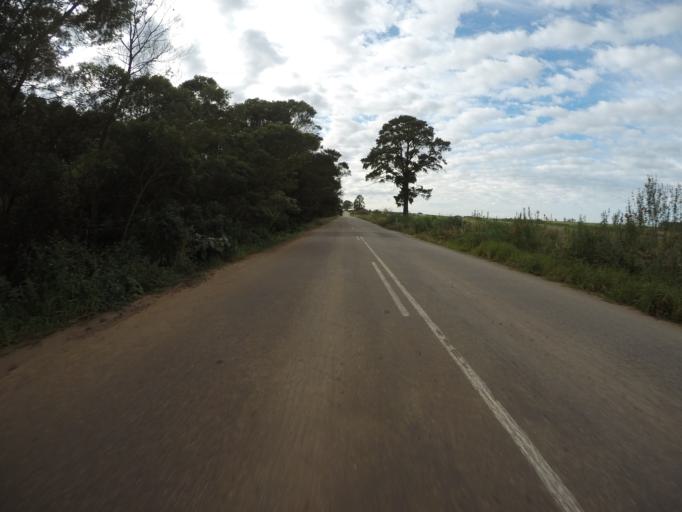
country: ZA
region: Eastern Cape
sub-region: Cacadu District Municipality
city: Kareedouw
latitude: -34.0089
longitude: 24.2684
